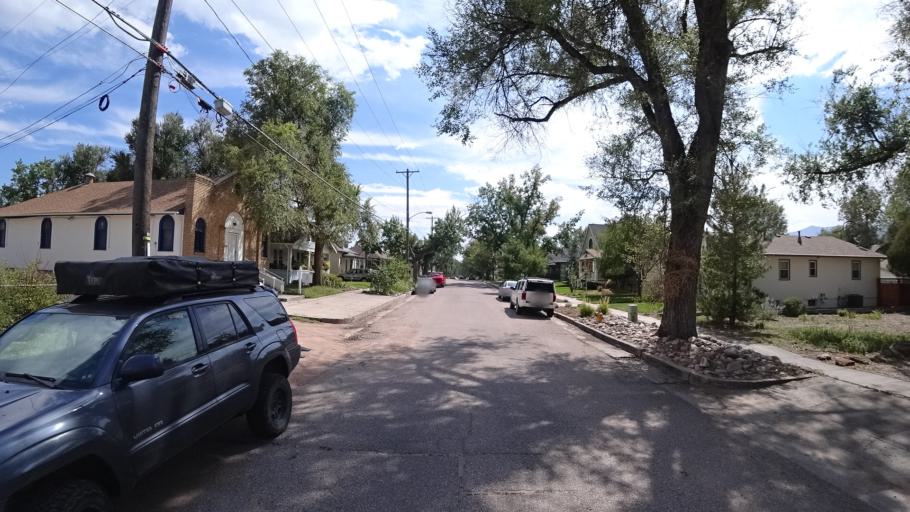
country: US
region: Colorado
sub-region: El Paso County
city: Colorado Springs
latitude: 38.8413
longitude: -104.8103
